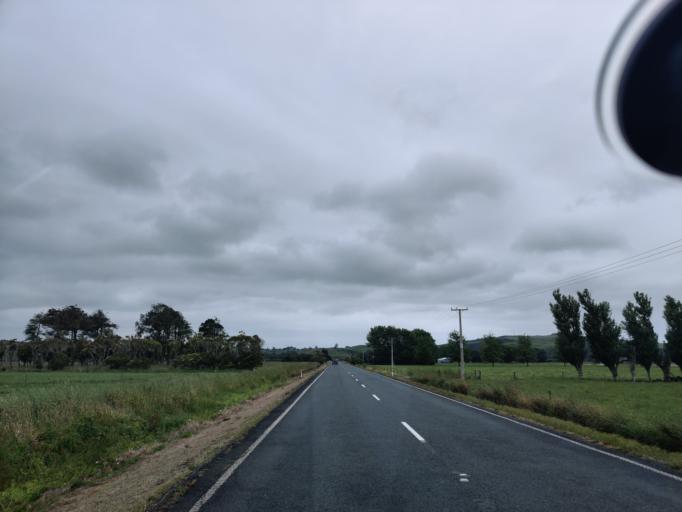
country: NZ
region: Northland
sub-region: Kaipara District
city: Dargaville
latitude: -36.1210
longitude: 174.0886
